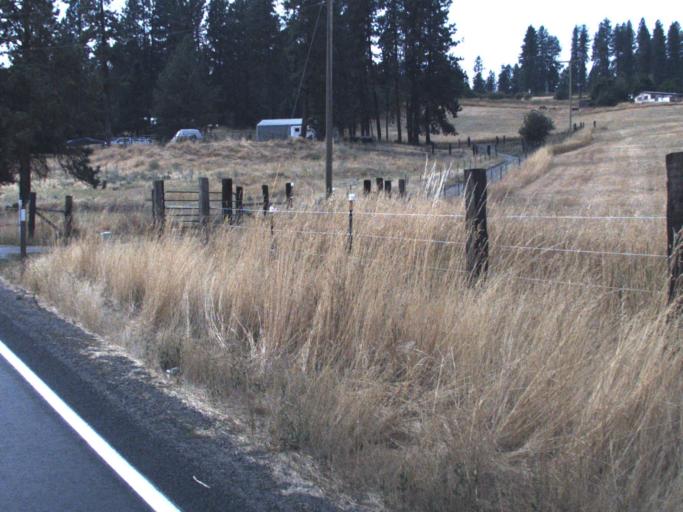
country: US
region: Washington
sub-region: Spokane County
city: Trentwood
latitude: 47.8021
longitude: -117.2327
